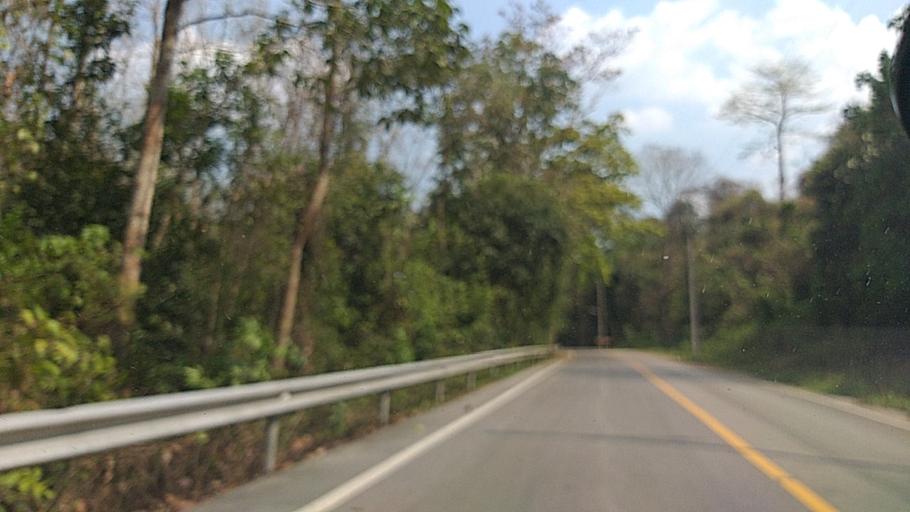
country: TH
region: Sara Buri
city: Saraburi
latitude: 14.4461
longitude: 100.9564
